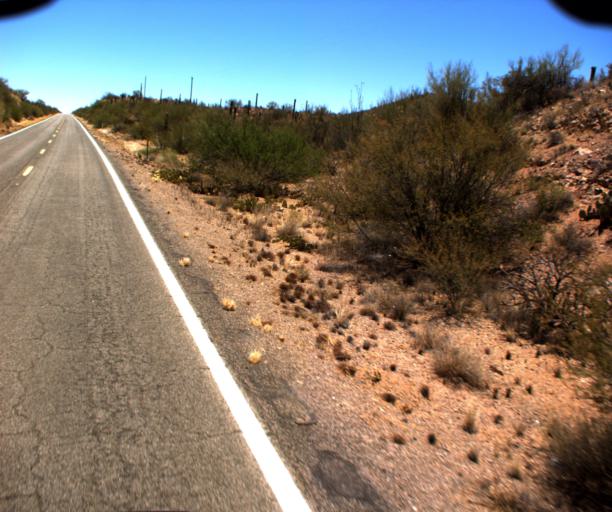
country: US
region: Arizona
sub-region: Pima County
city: Sells
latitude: 32.1749
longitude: -112.1817
